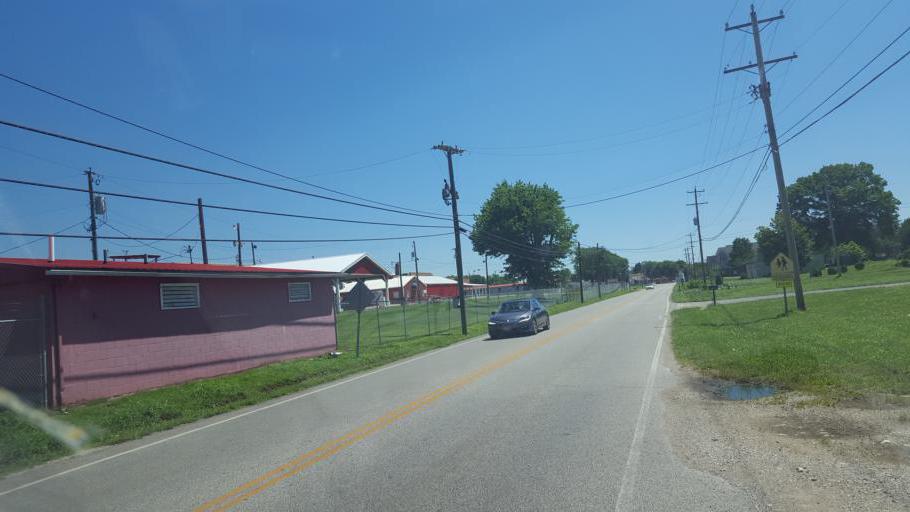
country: US
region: West Virginia
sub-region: Cabell County
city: Pea Ridge
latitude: 38.4419
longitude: -82.3609
